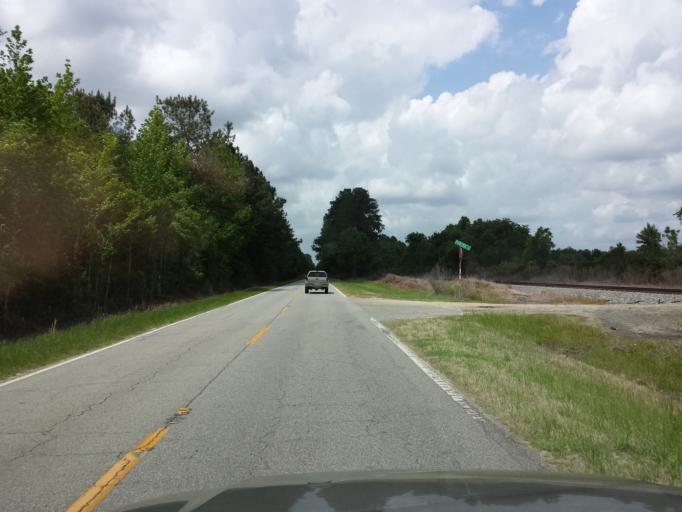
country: US
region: Georgia
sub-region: Echols County
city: Statenville
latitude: 30.6694
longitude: -83.1642
